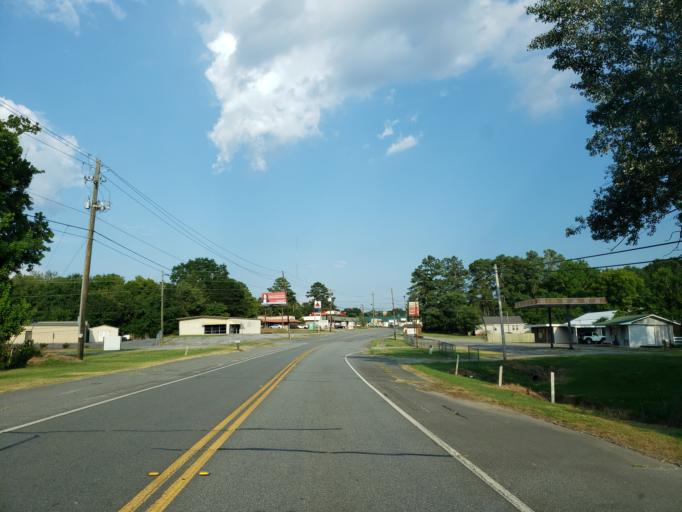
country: US
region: Georgia
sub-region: Polk County
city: Rockmart
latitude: 34.0055
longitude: -85.0658
